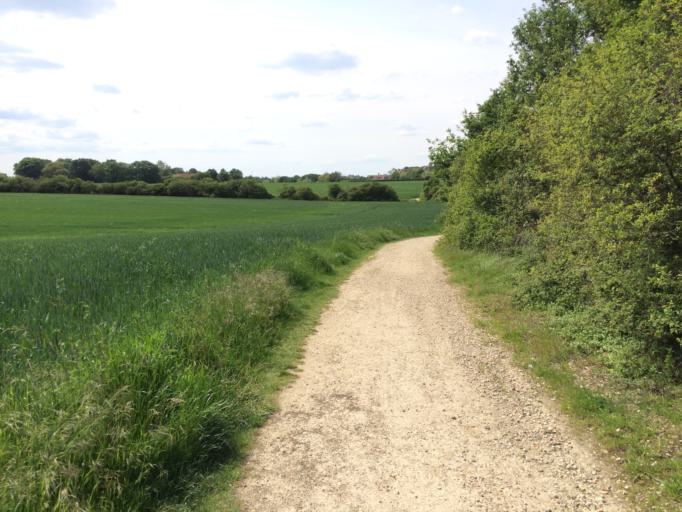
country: FR
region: Ile-de-France
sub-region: Departement de l'Essonne
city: Vauhallan
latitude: 48.7256
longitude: 2.2154
